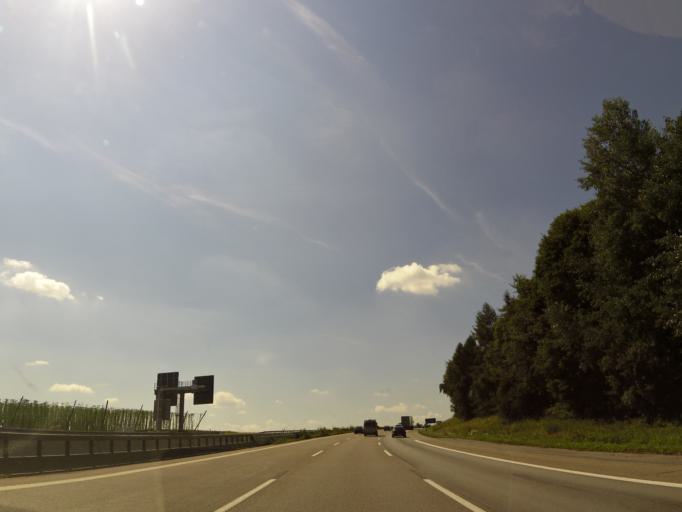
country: DE
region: Bavaria
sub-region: Upper Bavaria
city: Wolnzach
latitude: 48.5775
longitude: 11.5923
